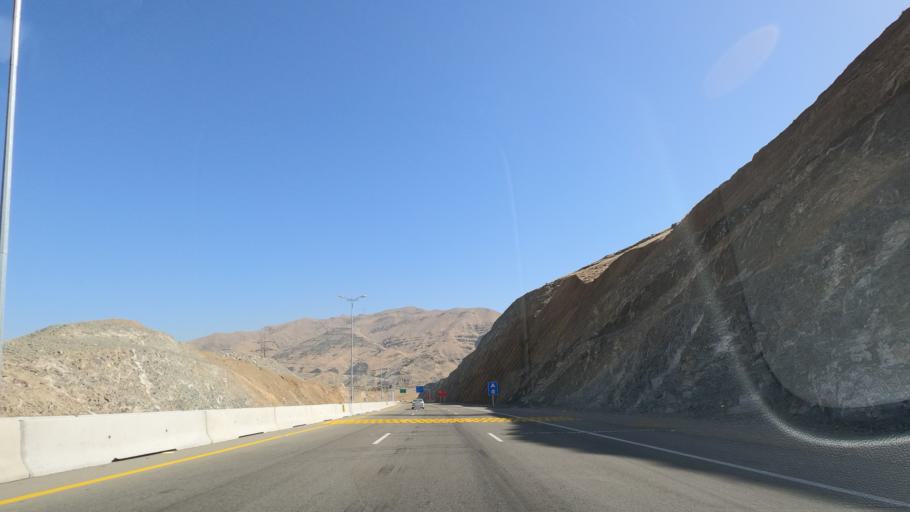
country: IR
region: Alborz
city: Karaj
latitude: 35.8168
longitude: 51.0379
